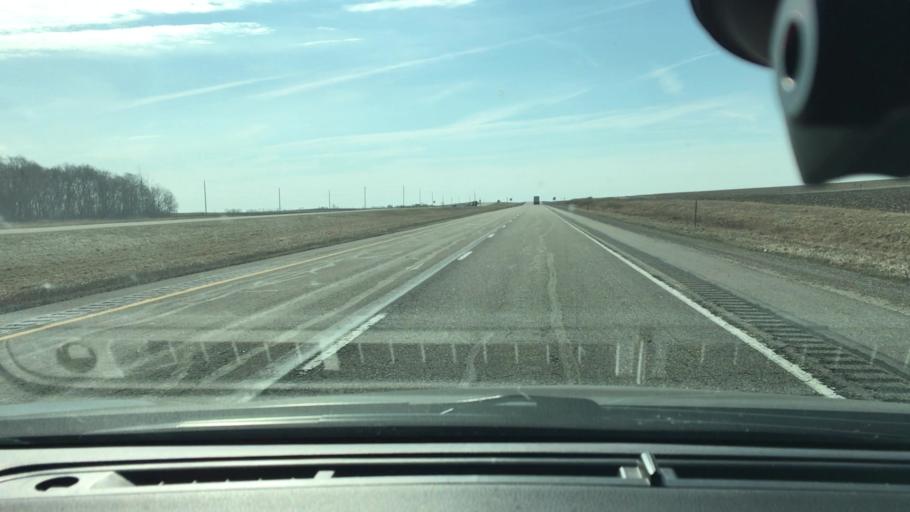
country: US
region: Iowa
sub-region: Chickasaw County
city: Nashua
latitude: 42.9929
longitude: -92.5961
